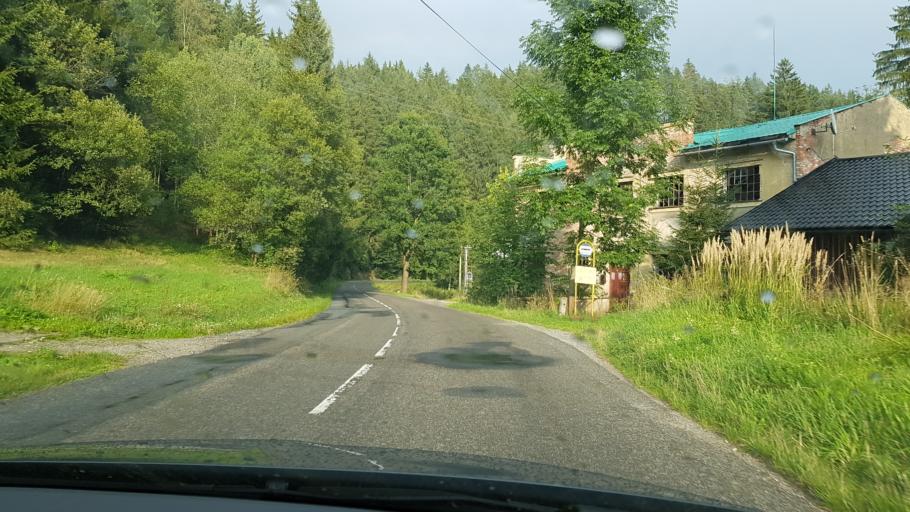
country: CZ
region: Olomoucky
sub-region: Okres Sumperk
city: Hanusovice
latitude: 50.0919
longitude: 16.8753
